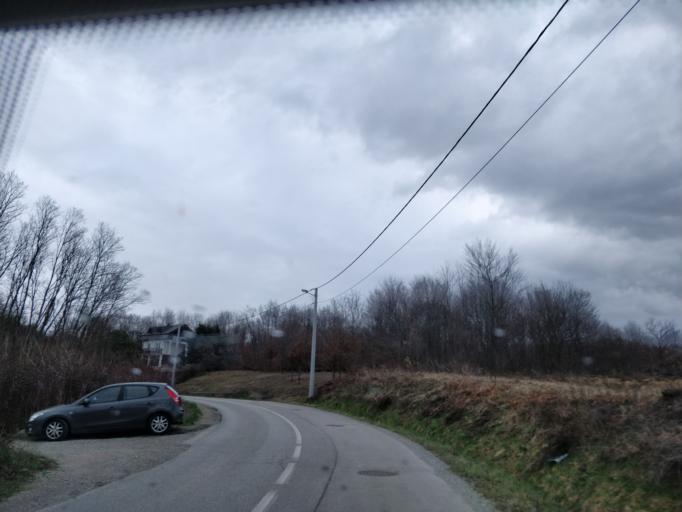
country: HR
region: Zagrebacka
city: Jakovlje
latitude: 45.9248
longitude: 15.9041
